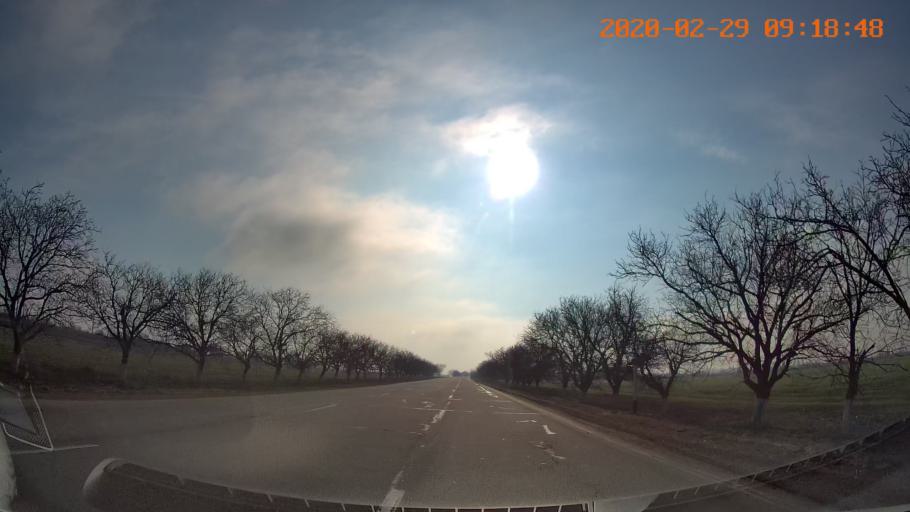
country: MD
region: Telenesti
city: Pervomaisc
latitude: 46.7700
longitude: 29.9299
